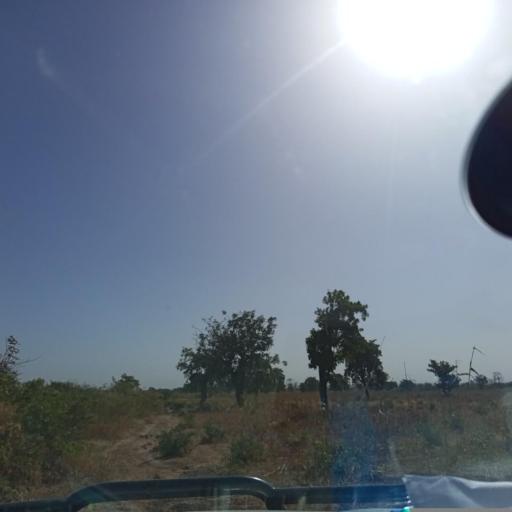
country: ML
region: Koulikoro
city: Koulikoro
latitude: 12.6854
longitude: -7.3079
